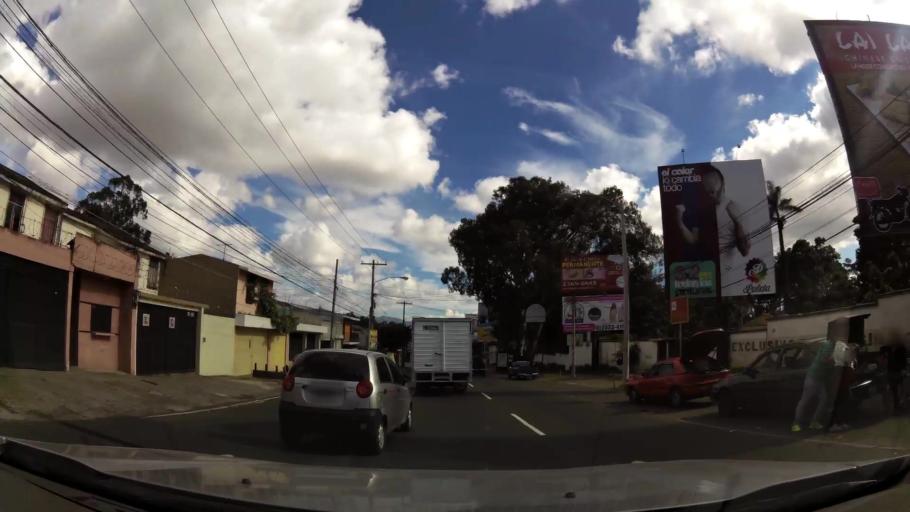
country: GT
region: Guatemala
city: Mixco
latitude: 14.5977
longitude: -90.5641
